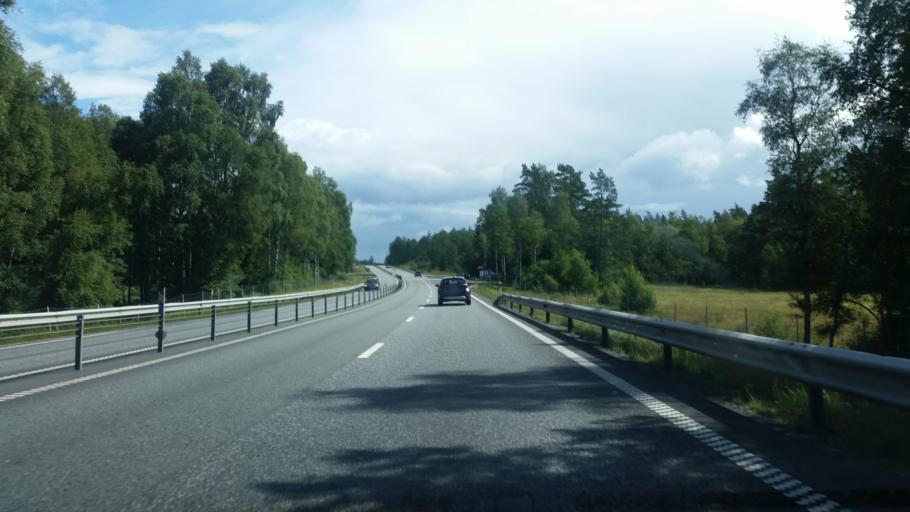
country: SE
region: Joenkoeping
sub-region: Mullsjo Kommun
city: Mullsjoe
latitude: 57.7665
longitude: 13.7801
